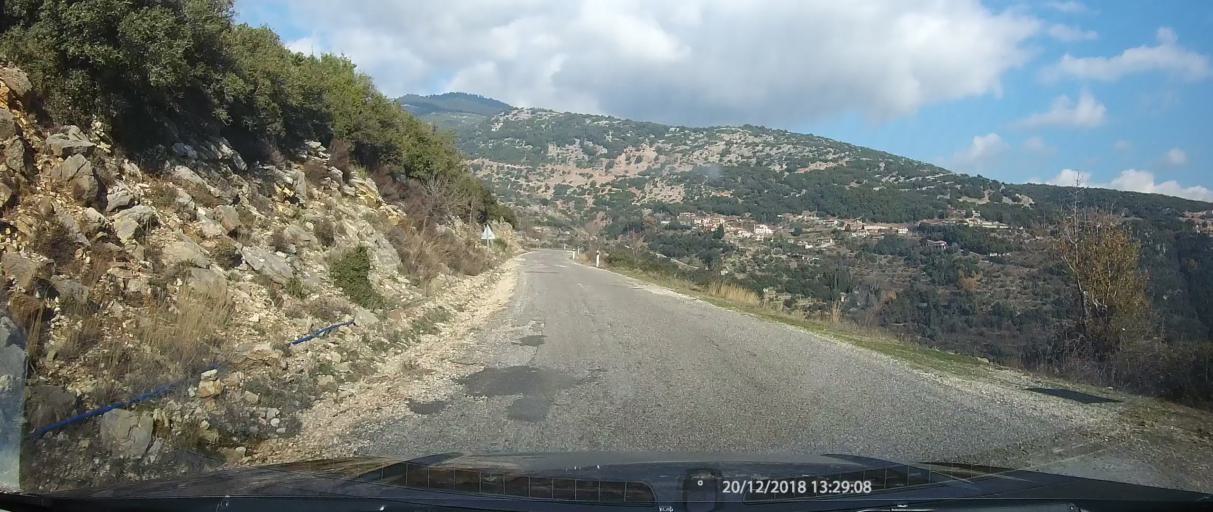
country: GR
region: West Greece
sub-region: Nomos Aitolias kai Akarnanias
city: Paravola
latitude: 38.6275
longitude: 21.5788
